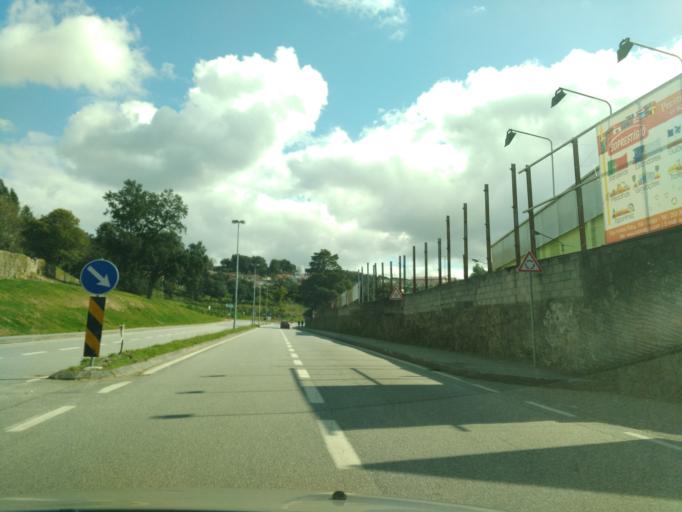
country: PT
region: Braga
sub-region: Braga
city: Braga
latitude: 41.5402
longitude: -8.4190
